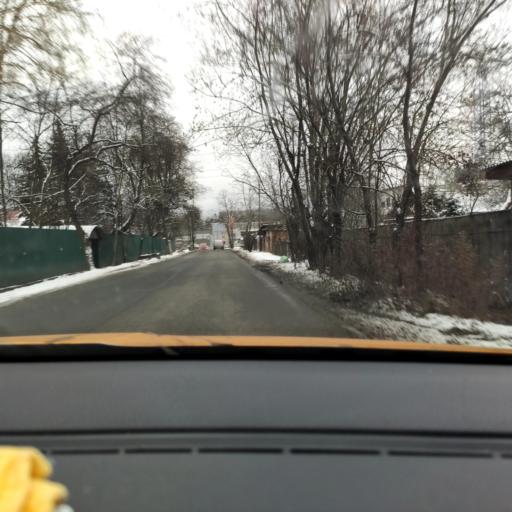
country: RU
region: Moskovskaya
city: Druzhba
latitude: 55.8894
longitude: 37.7442
